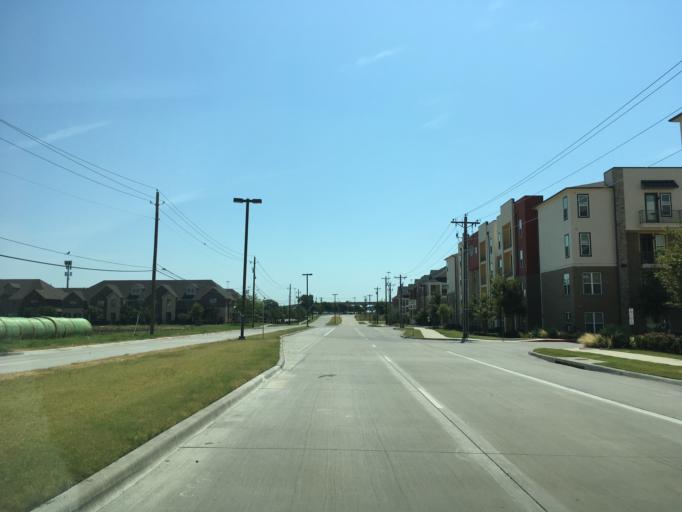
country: US
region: Texas
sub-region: Collin County
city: Fairview
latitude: 33.1590
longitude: -96.6526
